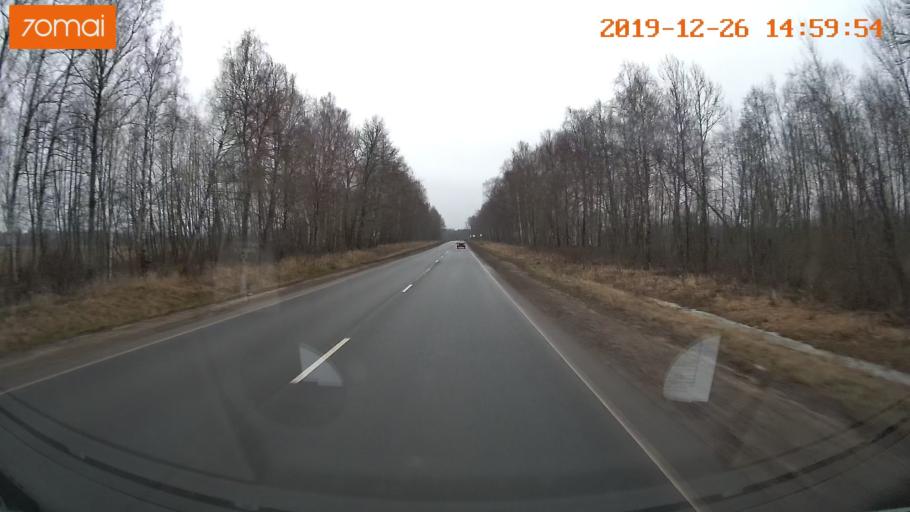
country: RU
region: Jaroslavl
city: Rybinsk
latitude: 58.2526
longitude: 38.8491
